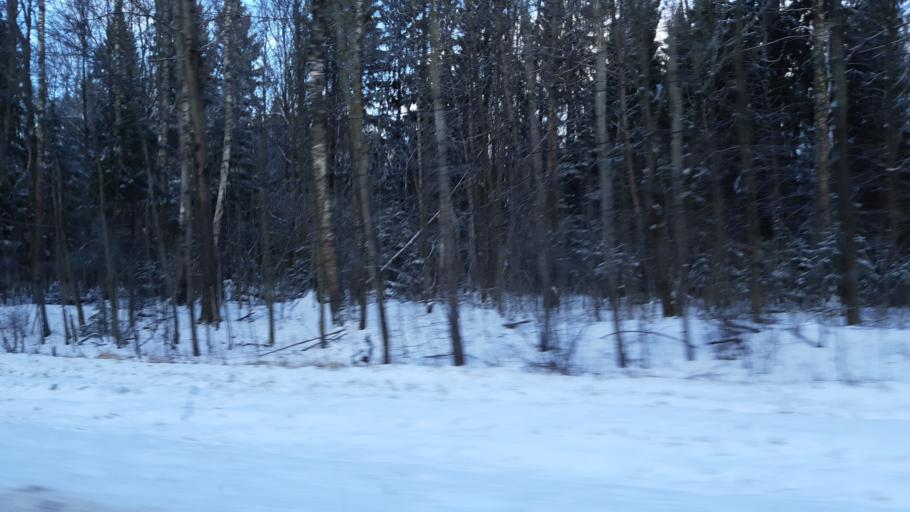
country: RU
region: Moskovskaya
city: Svatkovo
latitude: 56.3188
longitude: 38.2997
